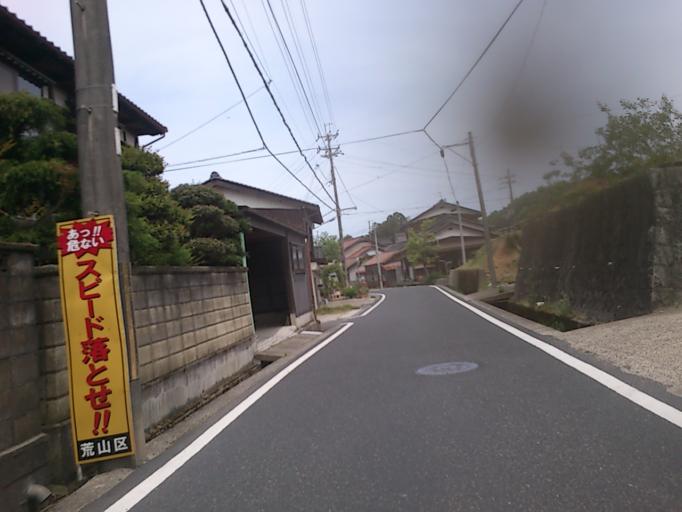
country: JP
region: Kyoto
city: Miyazu
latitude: 35.6176
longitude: 135.0835
